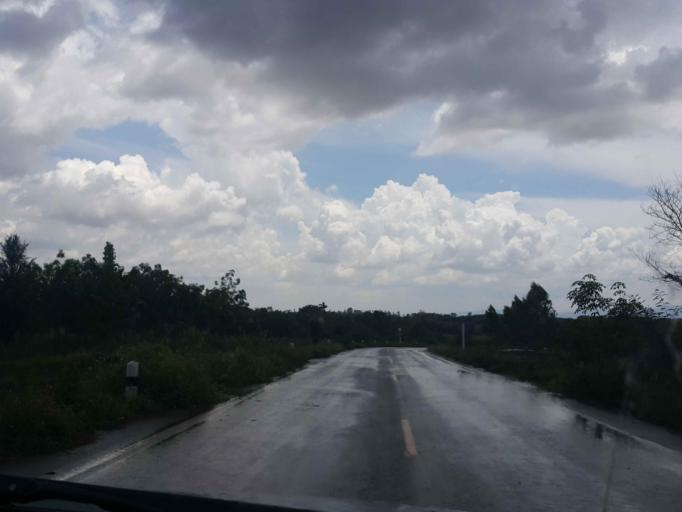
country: TH
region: Phayao
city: Dok Kham Tai
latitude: 19.0367
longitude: 99.9820
